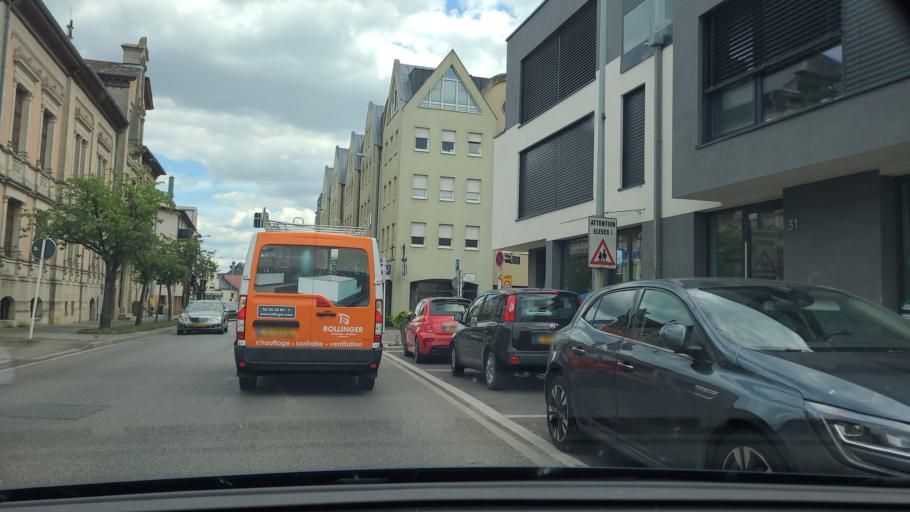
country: LU
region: Luxembourg
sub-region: Canton d'Esch-sur-Alzette
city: Bettembourg
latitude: 49.5209
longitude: 6.0989
